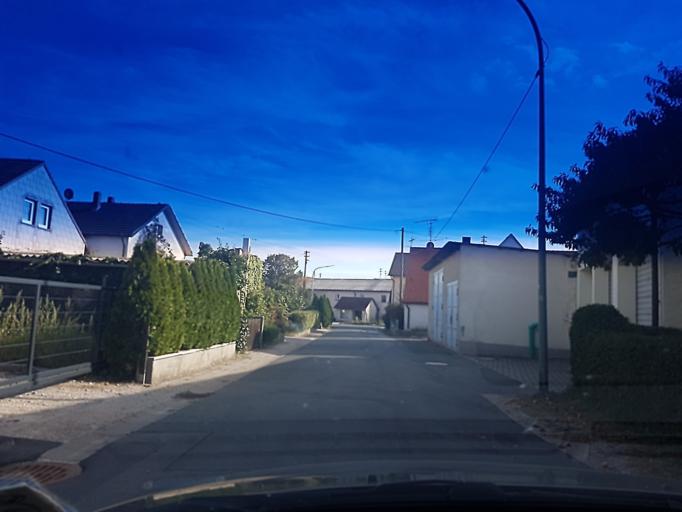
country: DE
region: Bavaria
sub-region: Regierungsbezirk Mittelfranken
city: Burghaslach
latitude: 49.7764
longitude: 10.5446
